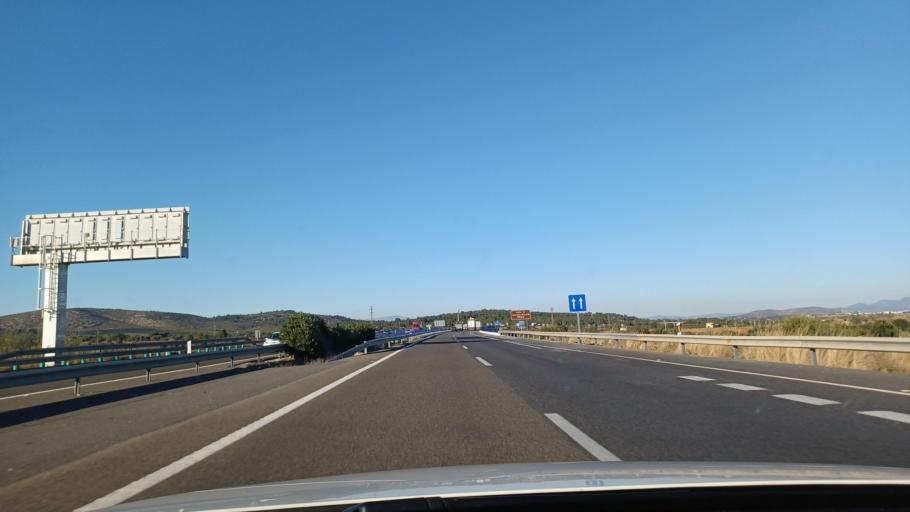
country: ES
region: Valencia
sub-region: Provincia de Castello
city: Peniscola
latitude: 40.4027
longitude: 0.3701
